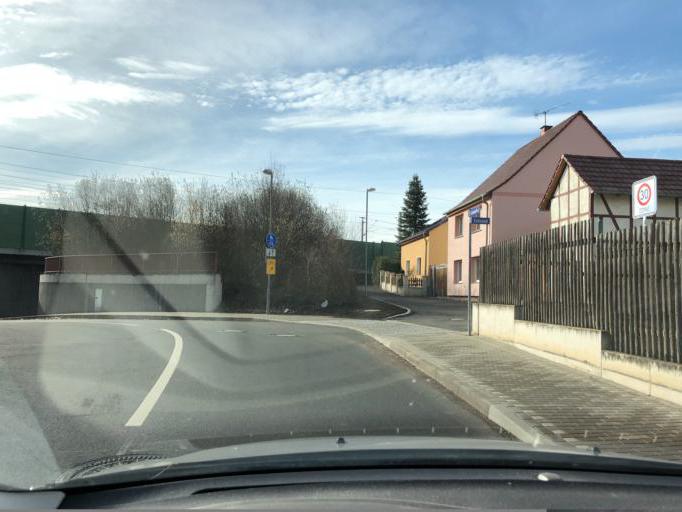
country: DE
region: Thuringia
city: Kleinmolsen
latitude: 50.9871
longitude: 11.1065
